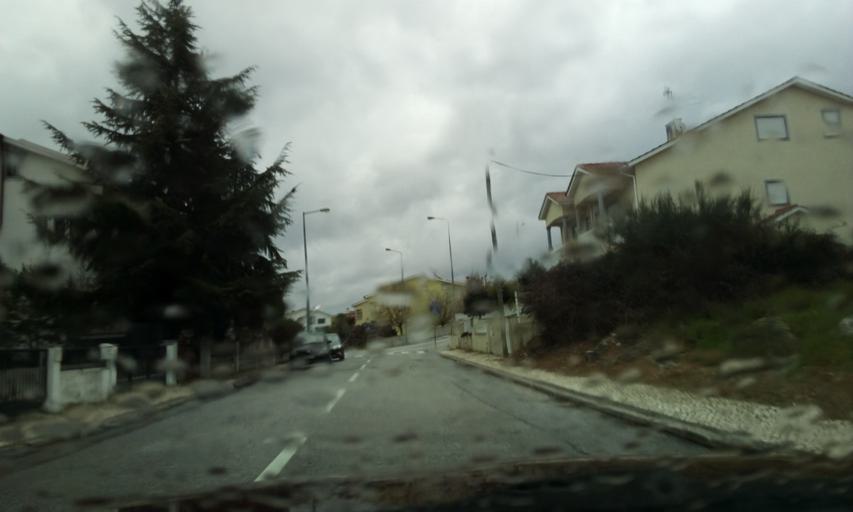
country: PT
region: Viseu
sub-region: Viseu
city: Rio de Loba
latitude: 40.6674
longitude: -7.8807
